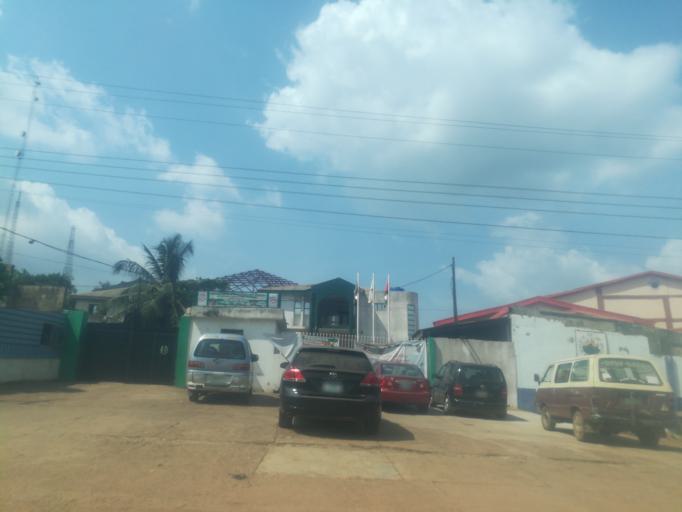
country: NG
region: Ogun
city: Abeokuta
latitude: 7.1759
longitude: 3.3853
